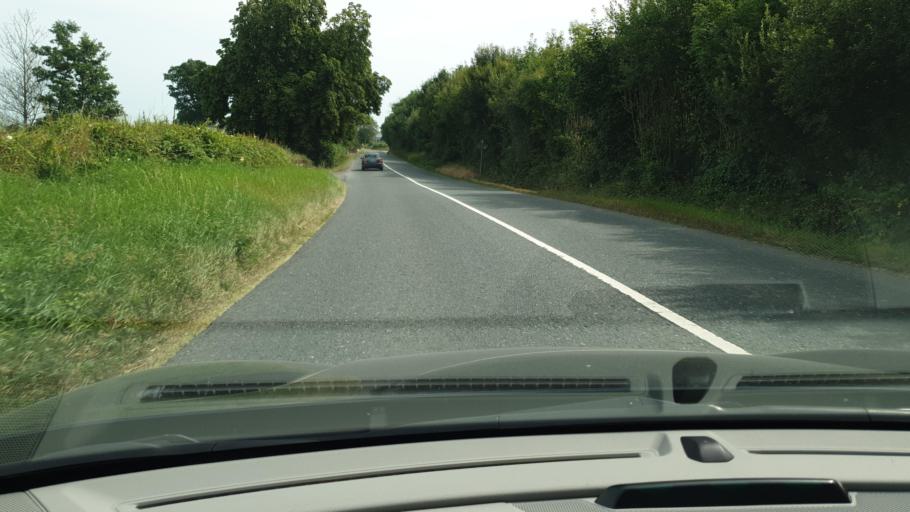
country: IE
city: Kentstown
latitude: 53.6229
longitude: -6.5172
